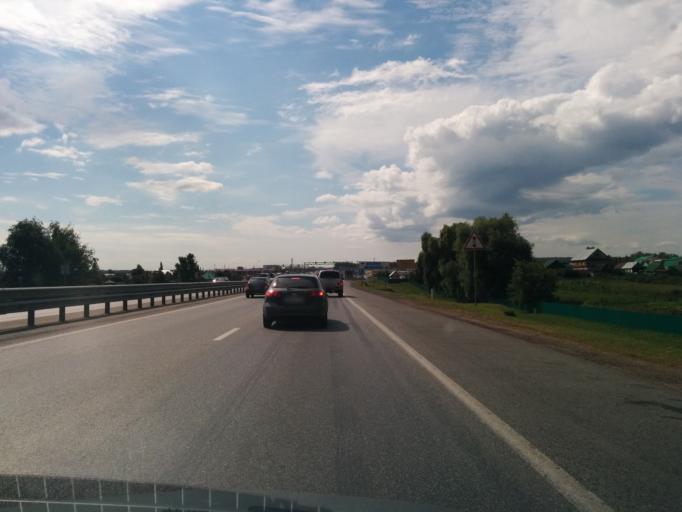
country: RU
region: Bashkortostan
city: Avdon
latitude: 54.5036
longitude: 55.9023
